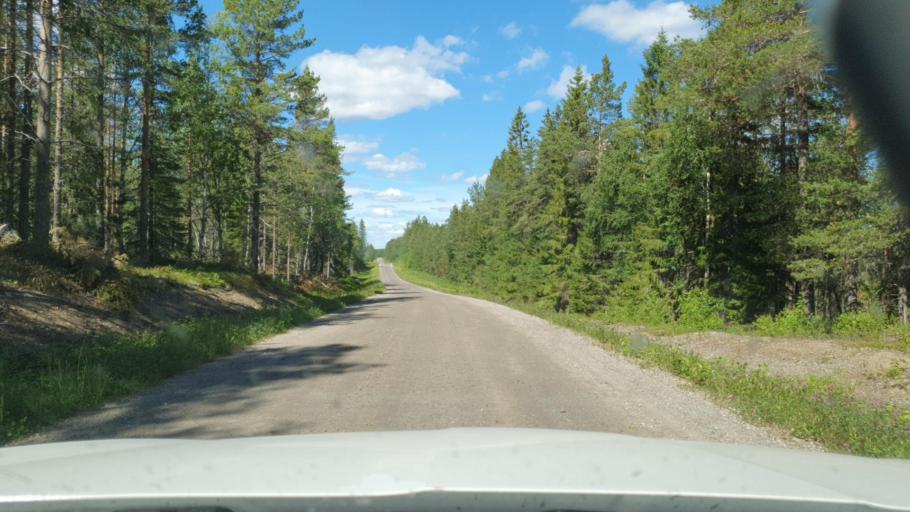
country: SE
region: Vaesterbotten
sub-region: Skelleftea Kommun
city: Byske
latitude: 65.1395
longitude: 21.1830
